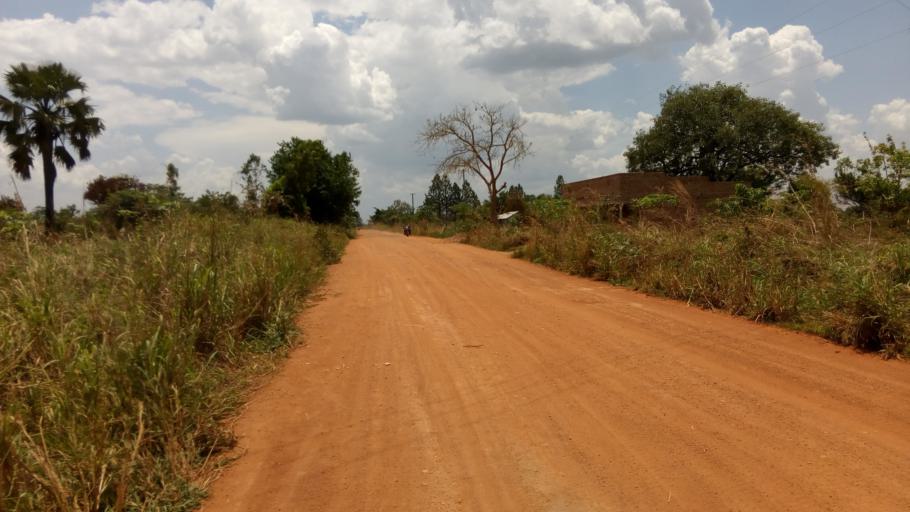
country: UG
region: Northern Region
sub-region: Gulu District
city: Gulu
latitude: 2.7853
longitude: 32.3538
